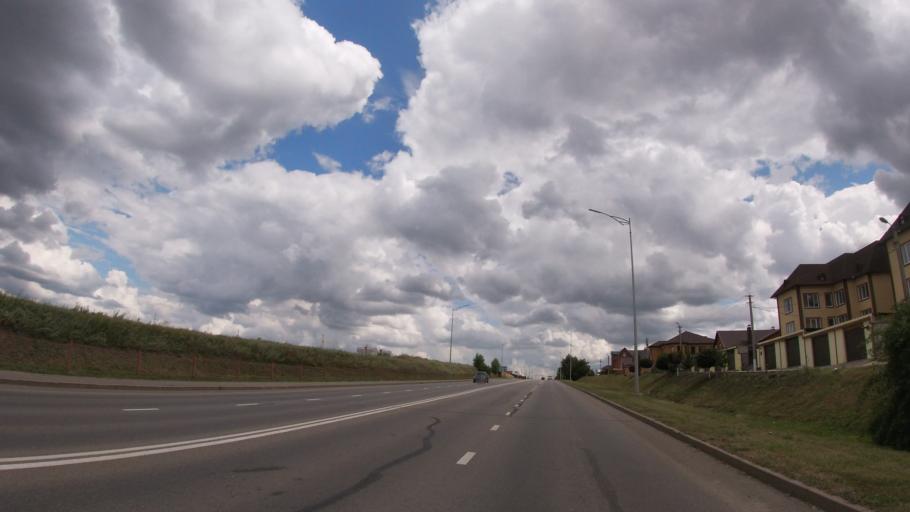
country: RU
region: Belgorod
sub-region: Belgorodskiy Rayon
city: Belgorod
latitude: 50.5508
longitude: 36.5550
